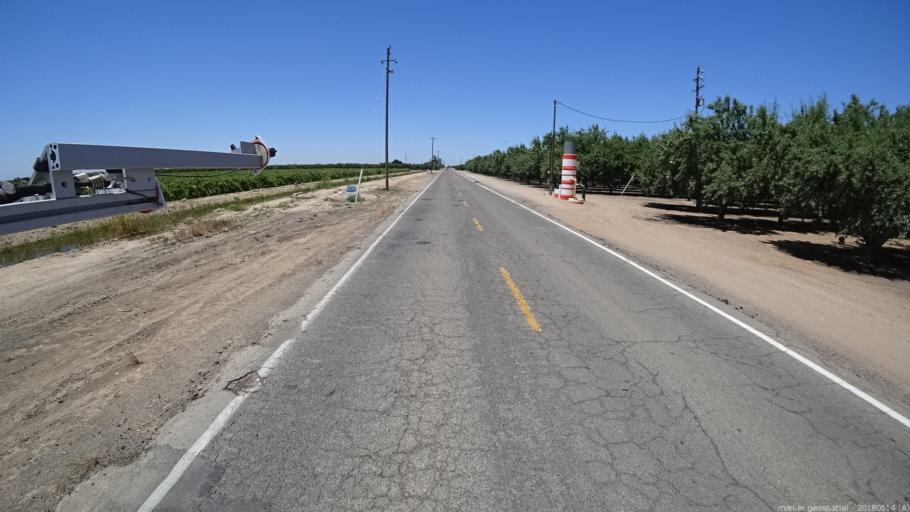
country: US
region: California
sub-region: Madera County
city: Fairmead
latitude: 37.0183
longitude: -120.1581
